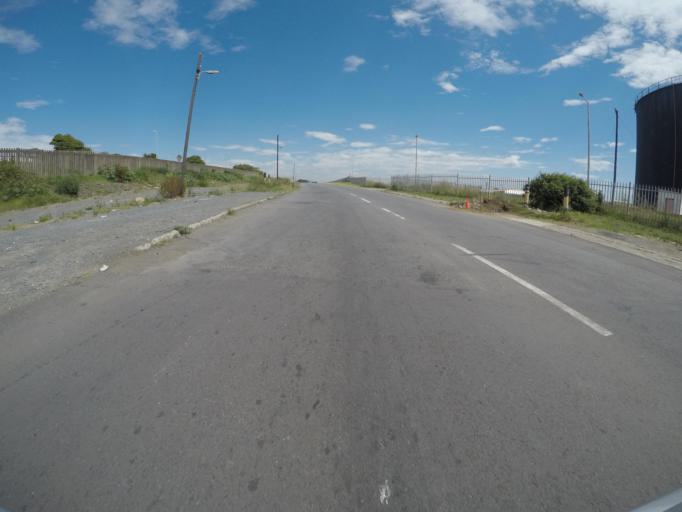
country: ZA
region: Eastern Cape
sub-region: Buffalo City Metropolitan Municipality
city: East London
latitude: -33.0291
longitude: 27.9060
